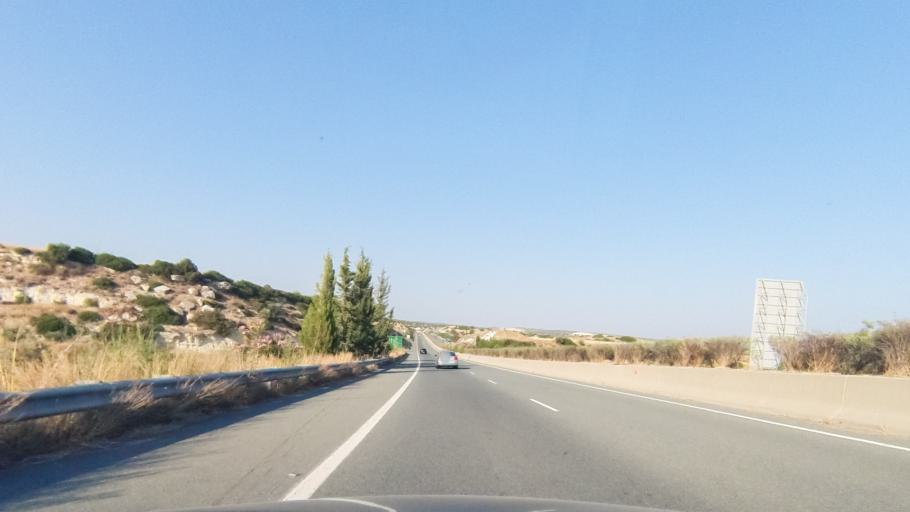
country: CY
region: Limassol
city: Pissouri
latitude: 34.6825
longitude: 32.7687
